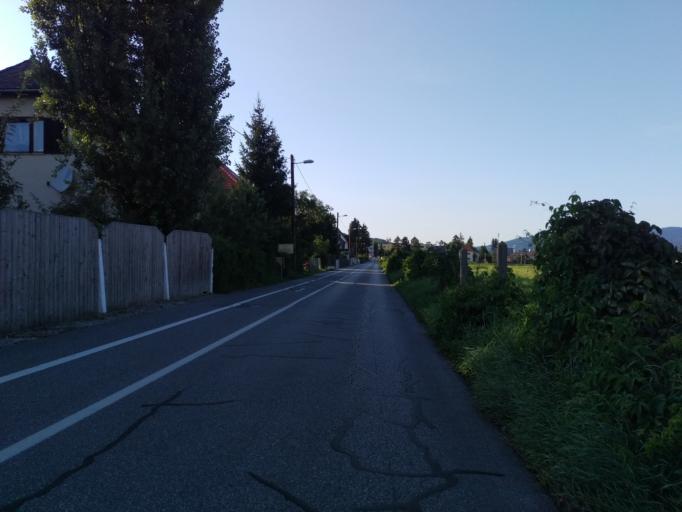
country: AT
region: Styria
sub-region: Graz Stadt
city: Wetzelsdorf
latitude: 47.0512
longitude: 15.4188
